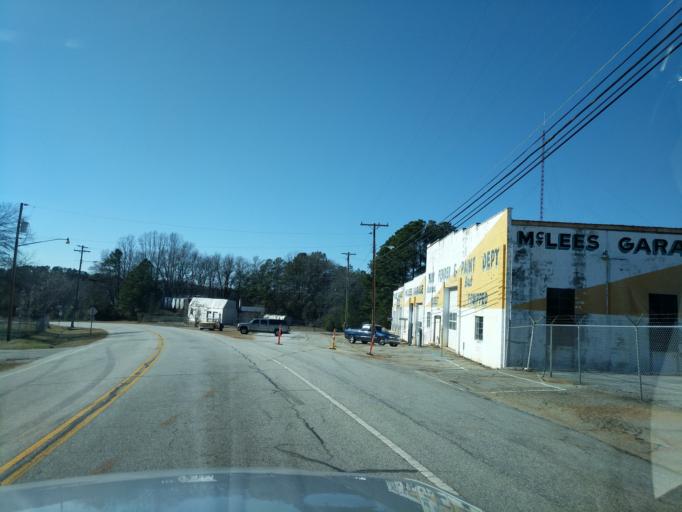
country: US
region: South Carolina
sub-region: Anderson County
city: Anderson
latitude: 34.4938
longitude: -82.6501
